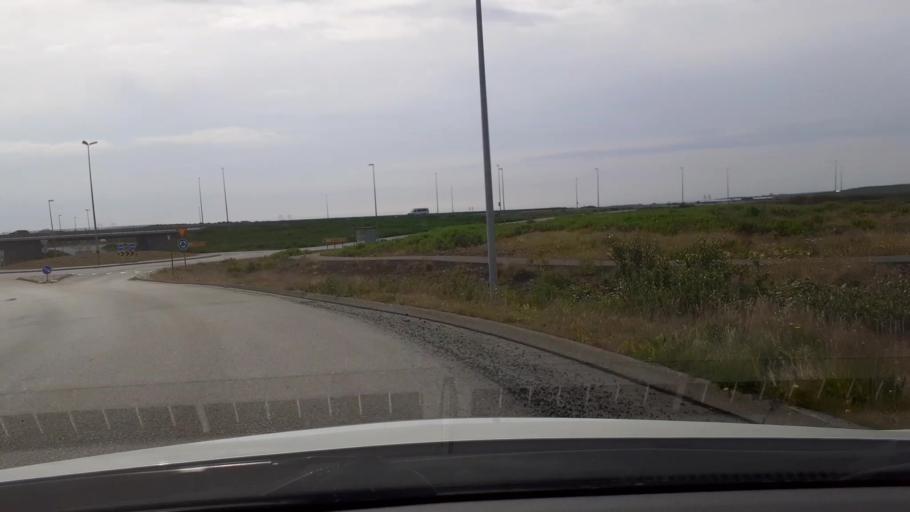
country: IS
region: Southern Peninsula
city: Reykjanesbaer
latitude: 63.9706
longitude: -22.5123
